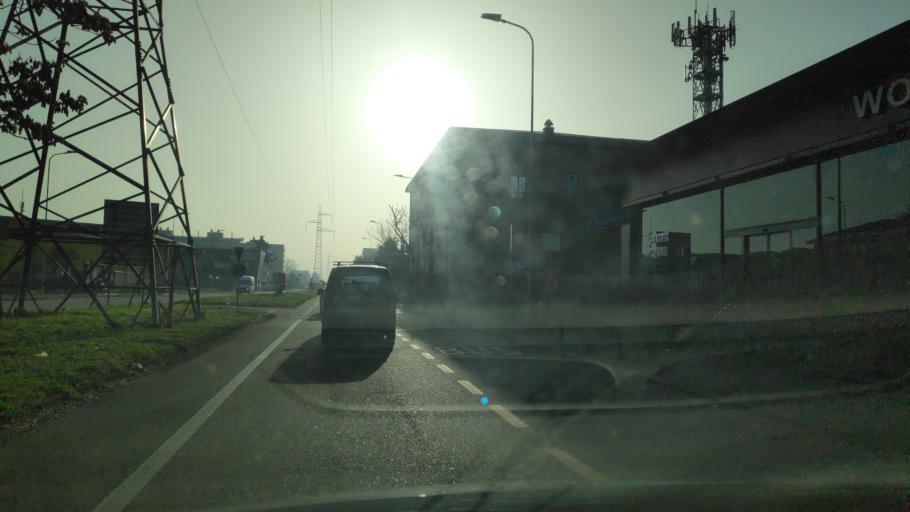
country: IT
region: Lombardy
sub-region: Citta metropolitana di Milano
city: Rozzano
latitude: 45.3940
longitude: 9.1555
